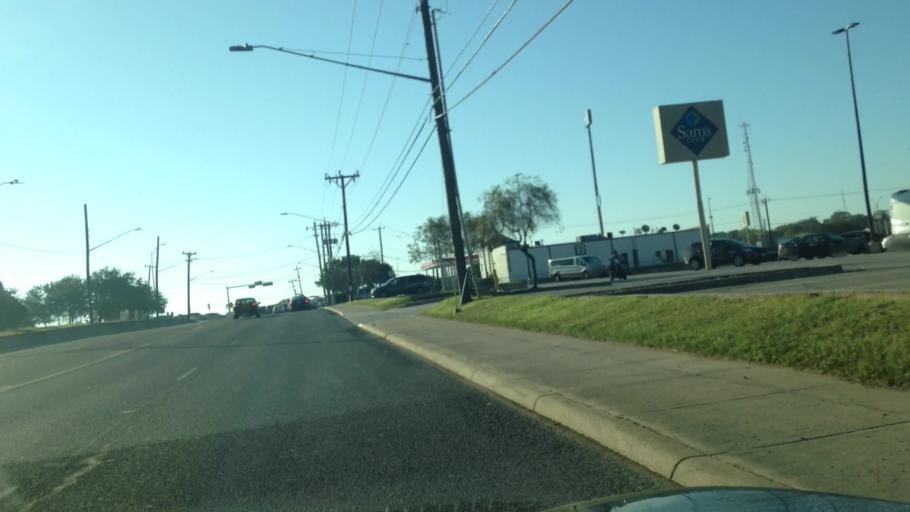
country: US
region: Texas
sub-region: Bexar County
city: Live Oak
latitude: 29.5541
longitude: -98.3567
